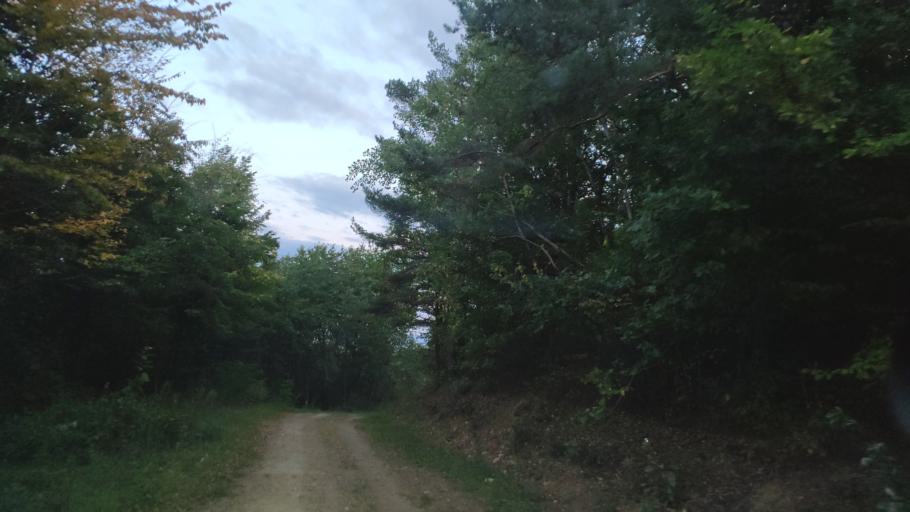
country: SK
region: Kosicky
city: Kosice
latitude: 48.7015
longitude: 21.2152
